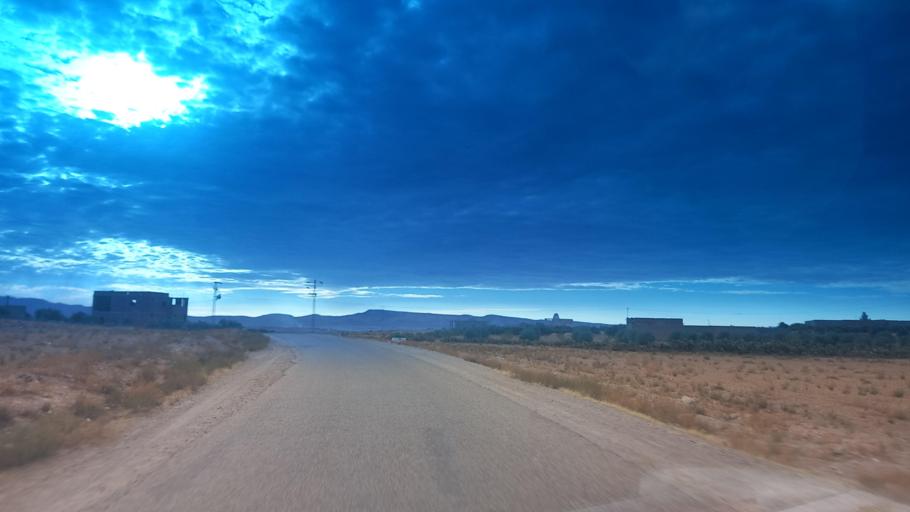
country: TN
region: Al Qasrayn
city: Sbiba
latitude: 35.3833
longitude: 9.0420
